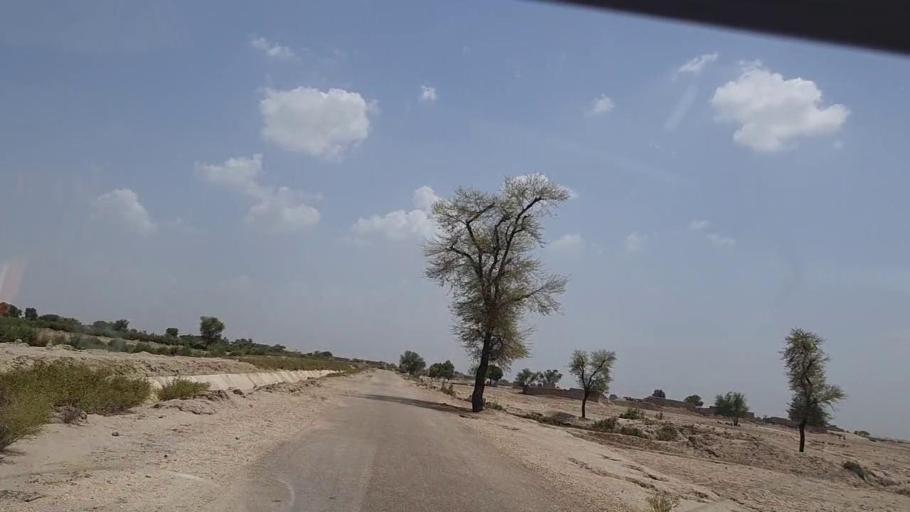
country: PK
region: Sindh
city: Bhan
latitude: 26.5253
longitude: 67.6343
